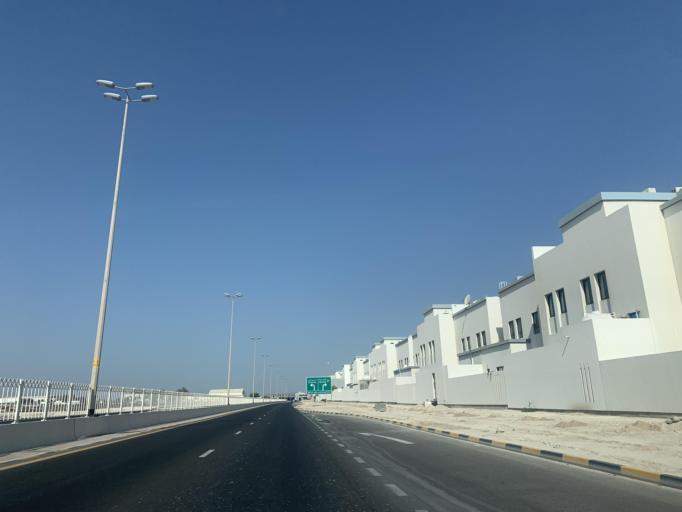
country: BH
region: Central Governorate
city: Madinat Hamad
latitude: 26.1290
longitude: 50.4833
